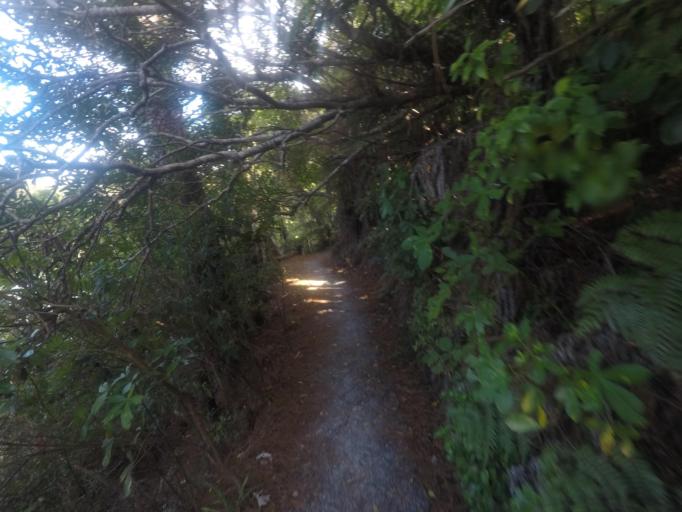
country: NZ
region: Auckland
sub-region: Auckland
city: Warkworth
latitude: -36.2874
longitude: 174.8078
